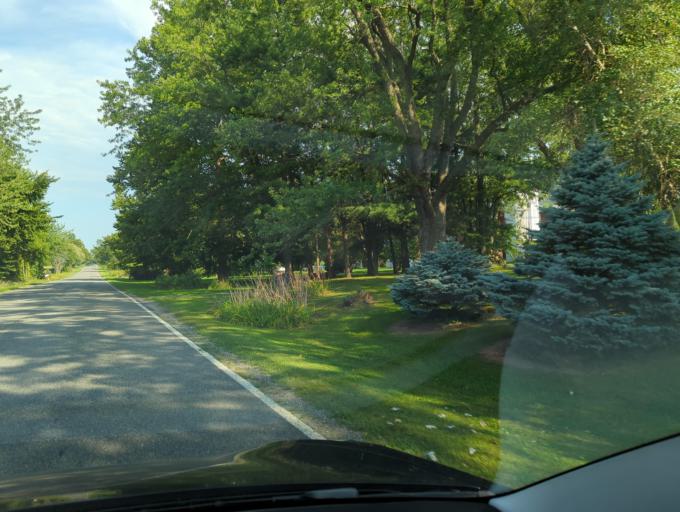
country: US
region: Michigan
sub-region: Ionia County
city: Ionia
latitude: 42.9297
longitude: -85.0942
